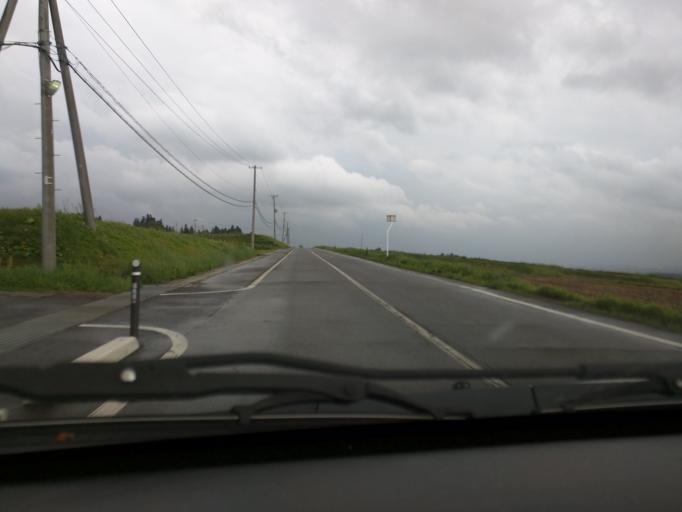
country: JP
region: Fukushima
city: Kitakata
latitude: 37.6283
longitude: 139.9360
